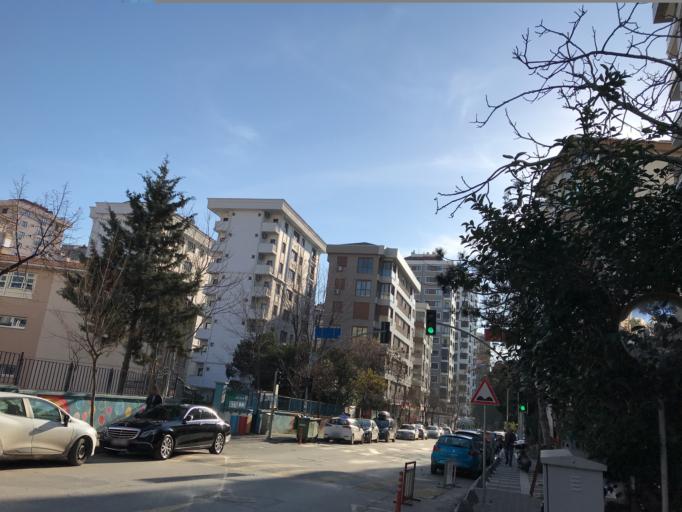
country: TR
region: Istanbul
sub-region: Atasehir
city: Atasehir
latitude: 40.9635
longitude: 29.0988
